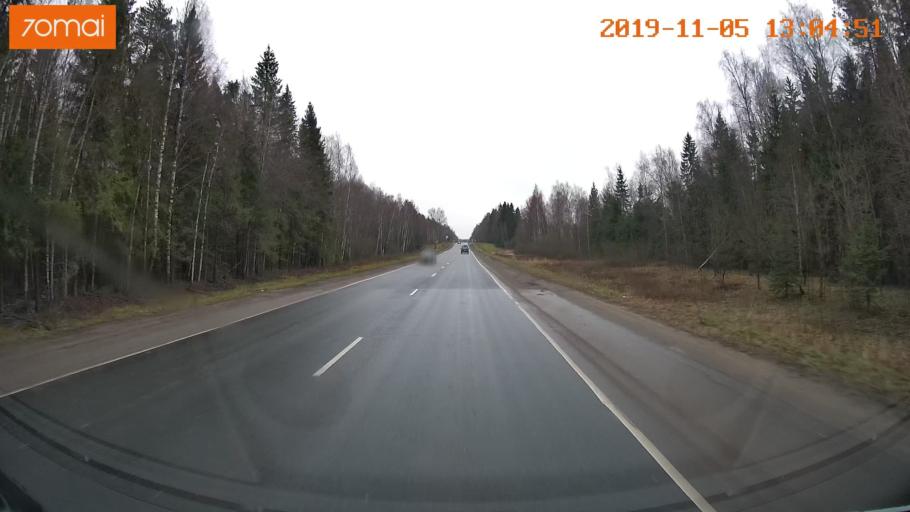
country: RU
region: Ivanovo
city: Kitovo
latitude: 56.8864
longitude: 41.2301
